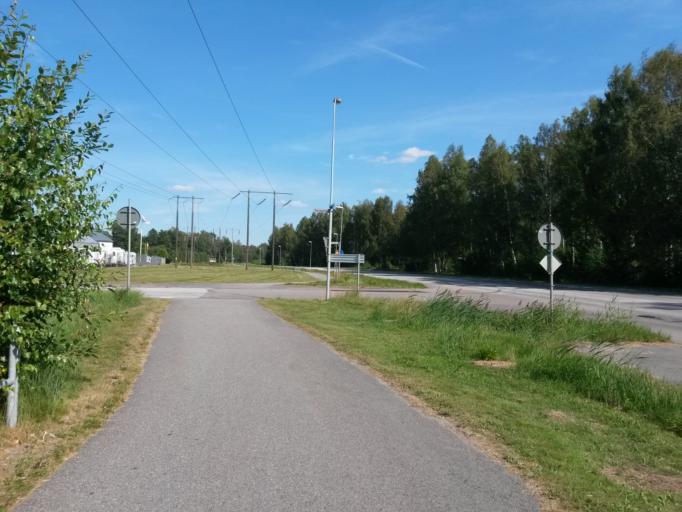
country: SE
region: Vaestra Goetaland
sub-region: Lidkopings Kommun
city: Lidkoping
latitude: 58.4957
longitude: 13.1892
